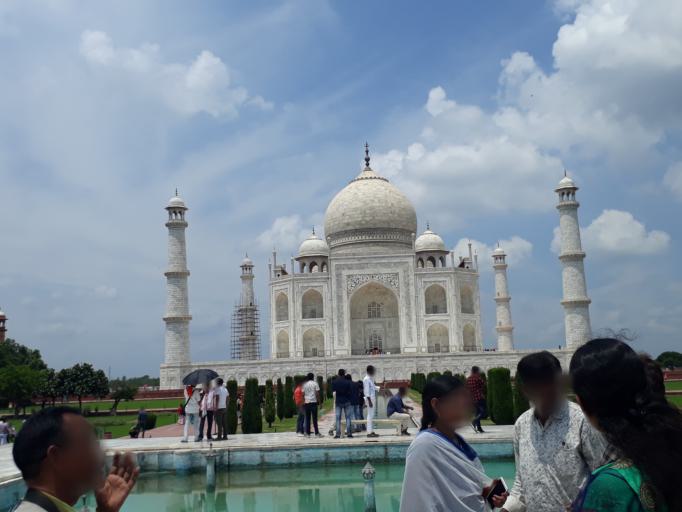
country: IN
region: Uttar Pradesh
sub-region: Agra
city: Agra
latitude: 27.1731
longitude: 78.0421
